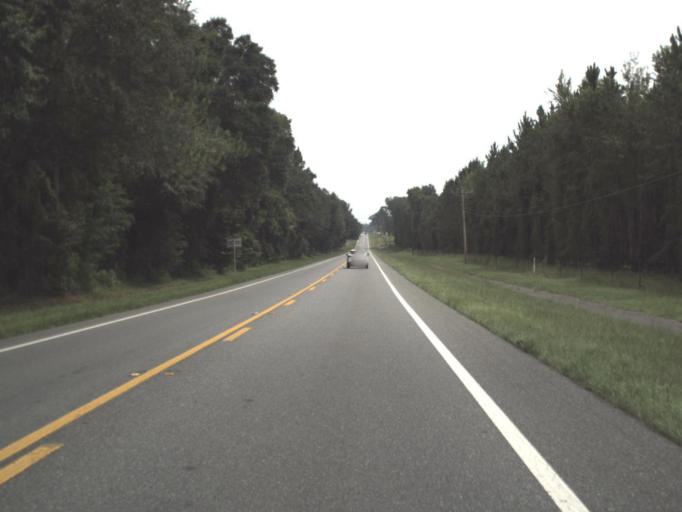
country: US
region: Florida
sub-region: Columbia County
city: Watertown
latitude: 30.0677
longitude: -82.6001
